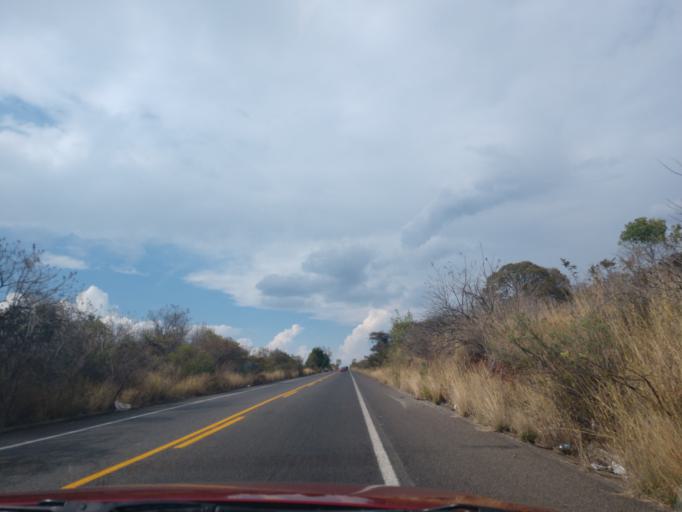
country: MX
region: Jalisco
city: La Manzanilla de la Paz
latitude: 20.0647
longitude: -103.1715
